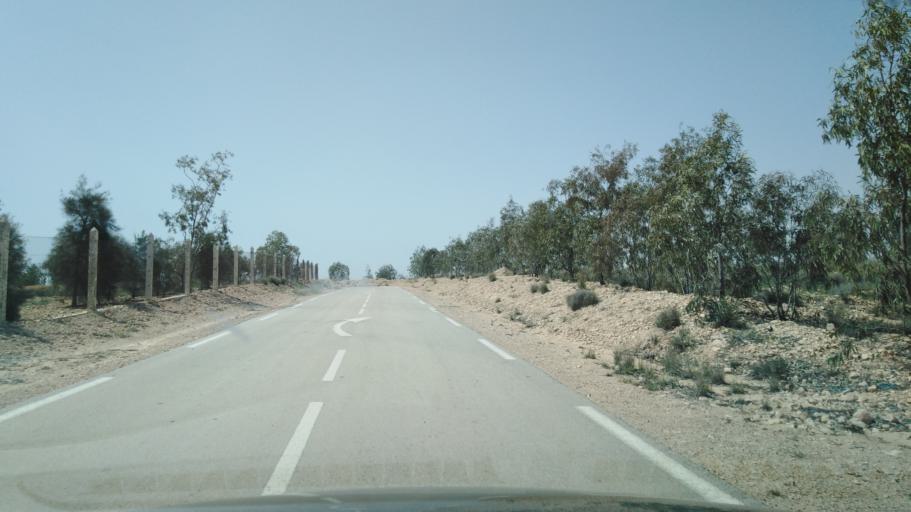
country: TN
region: Safaqis
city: Sfax
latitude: 34.7087
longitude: 10.5228
